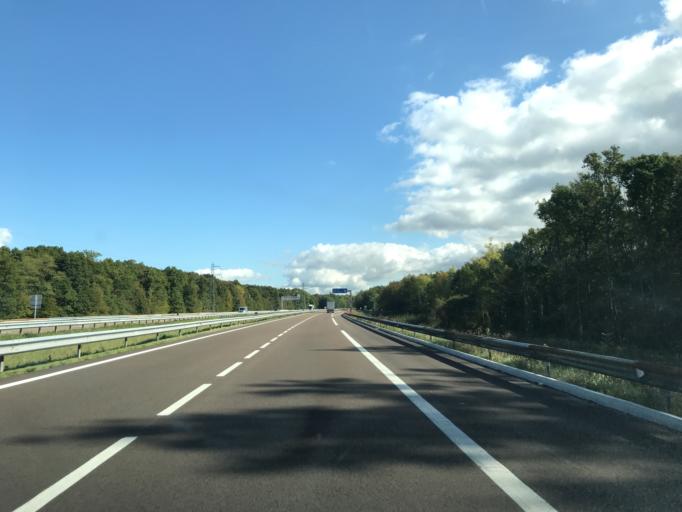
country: FR
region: Centre
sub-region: Departement du Loiret
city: Courtenay
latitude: 48.1087
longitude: 3.0101
